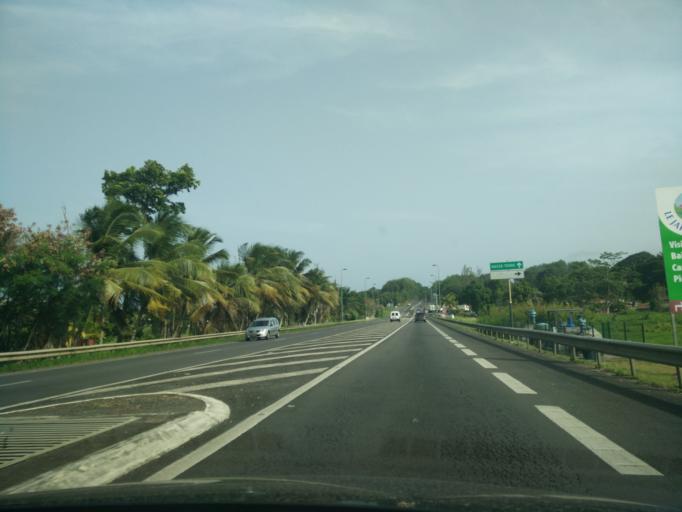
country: GP
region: Guadeloupe
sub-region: Guadeloupe
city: Petit-Bourg
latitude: 16.1502
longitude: -61.5841
